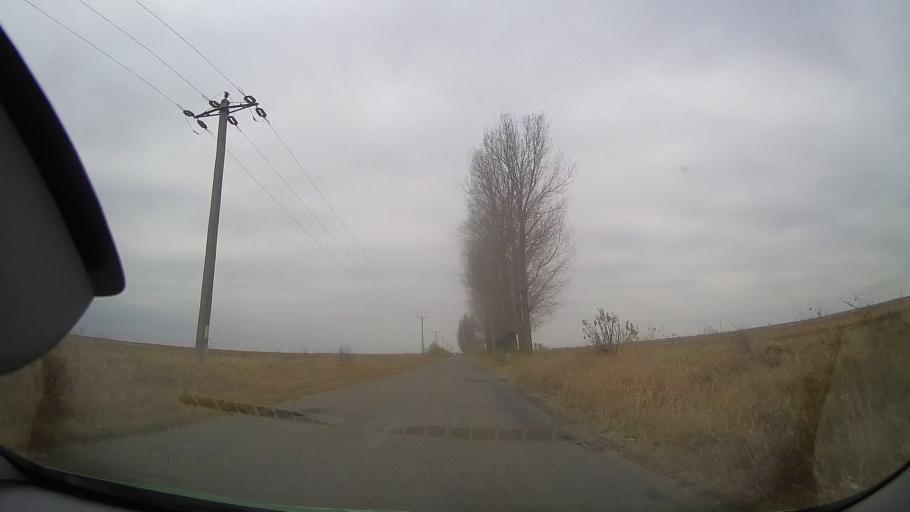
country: RO
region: Buzau
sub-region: Comuna Pogoanele
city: Pogoanele
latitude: 44.9588
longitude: 27.0196
